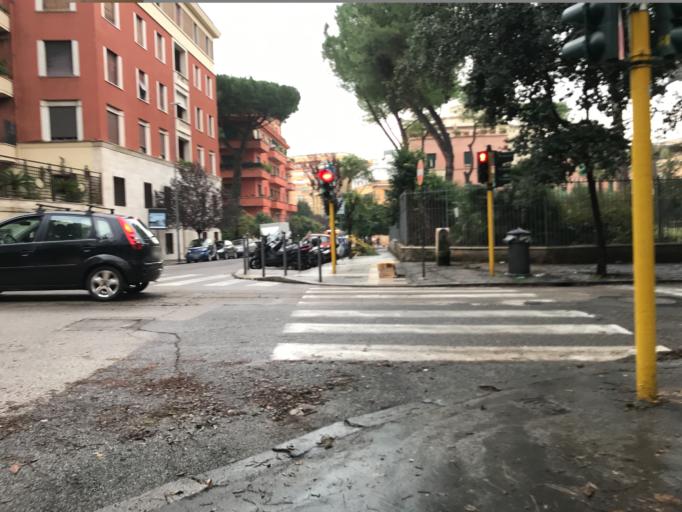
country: IT
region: Latium
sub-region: Citta metropolitana di Roma Capitale
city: Rome
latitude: 41.9138
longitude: 12.5154
